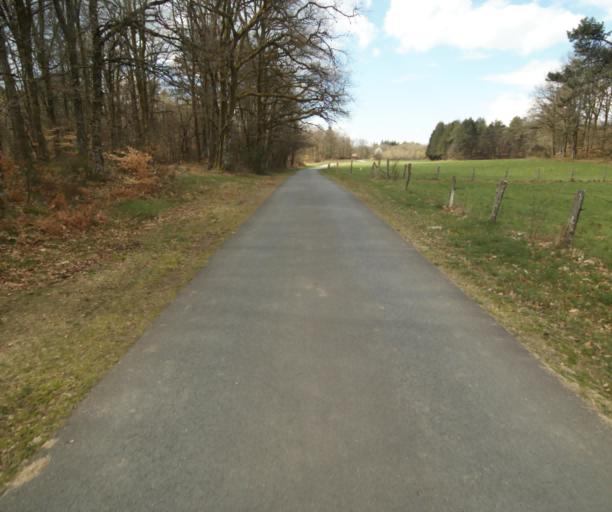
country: FR
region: Limousin
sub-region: Departement de la Correze
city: Correze
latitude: 45.2793
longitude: 1.9062
